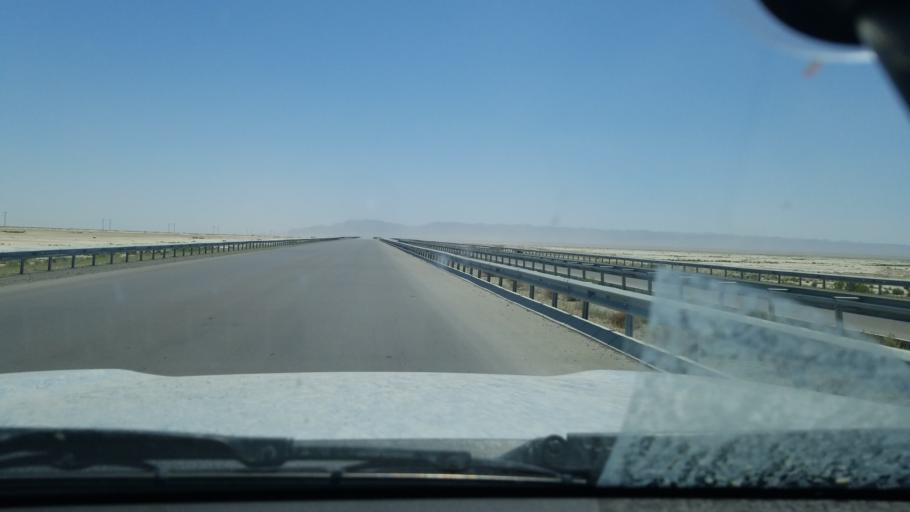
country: TM
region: Balkan
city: Gazanjyk
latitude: 39.2810
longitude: 55.2464
